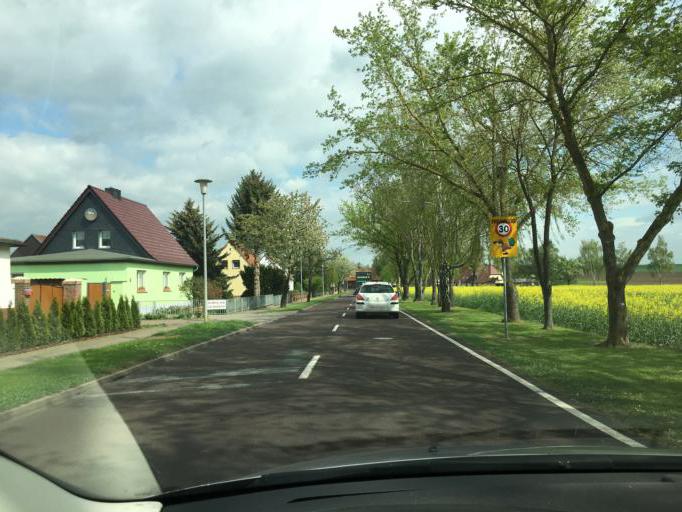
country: DE
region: Saxony-Anhalt
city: Giersleben
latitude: 51.7341
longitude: 11.5917
